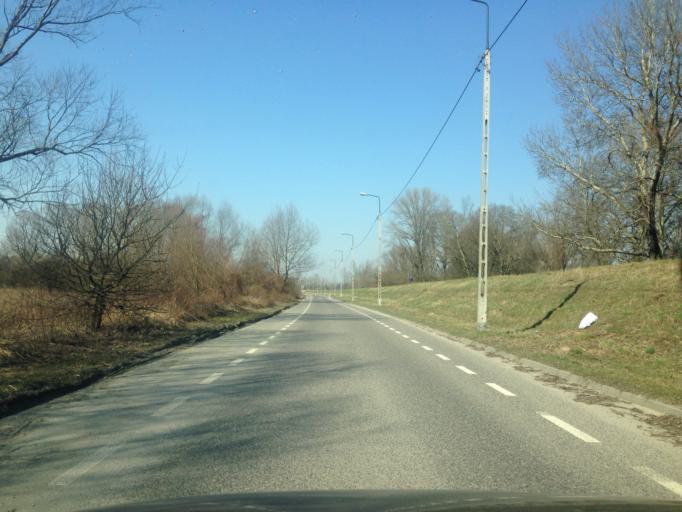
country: PL
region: Masovian Voivodeship
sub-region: Warszawa
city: Wilanow
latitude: 52.1863
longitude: 21.1073
